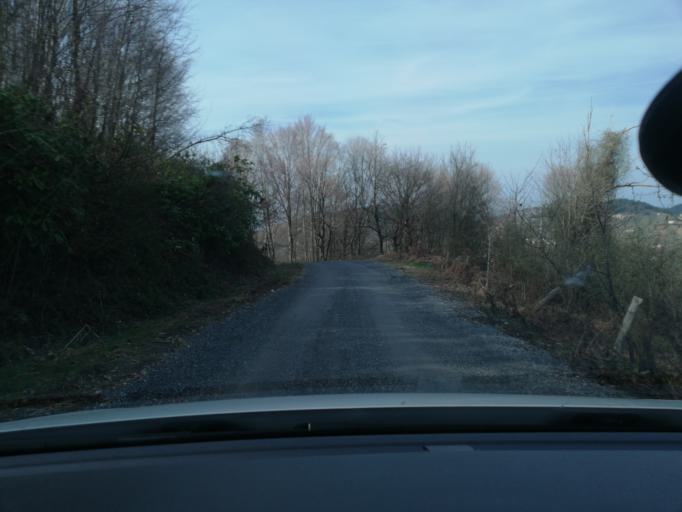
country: TR
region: Zonguldak
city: Kozlu
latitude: 41.3526
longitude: 31.6311
